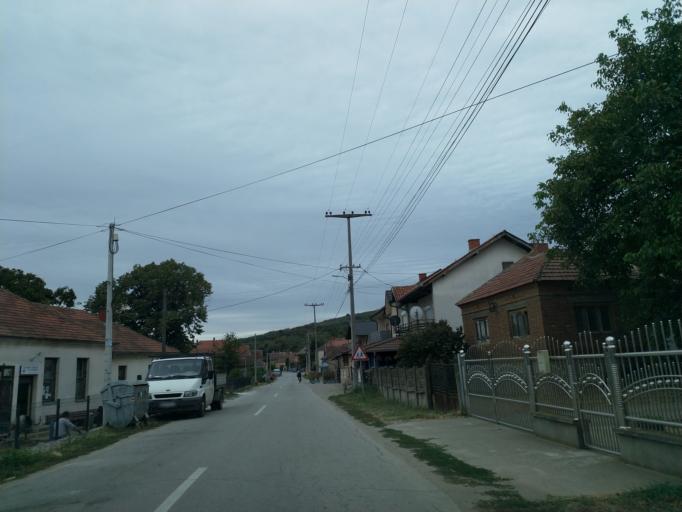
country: RS
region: Central Serbia
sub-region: Pomoravski Okrug
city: Cuprija
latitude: 43.8704
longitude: 21.3223
